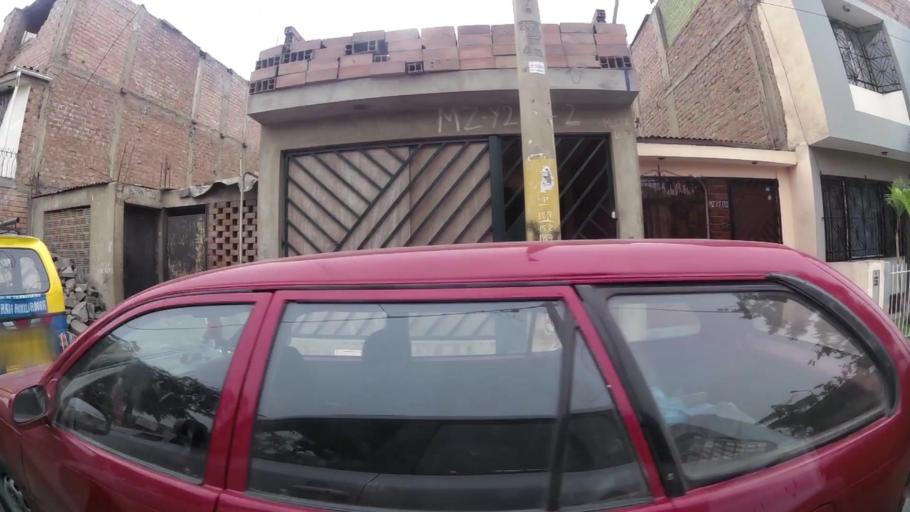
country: PE
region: Lima
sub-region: Lima
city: Surco
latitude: -12.1640
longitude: -76.9614
